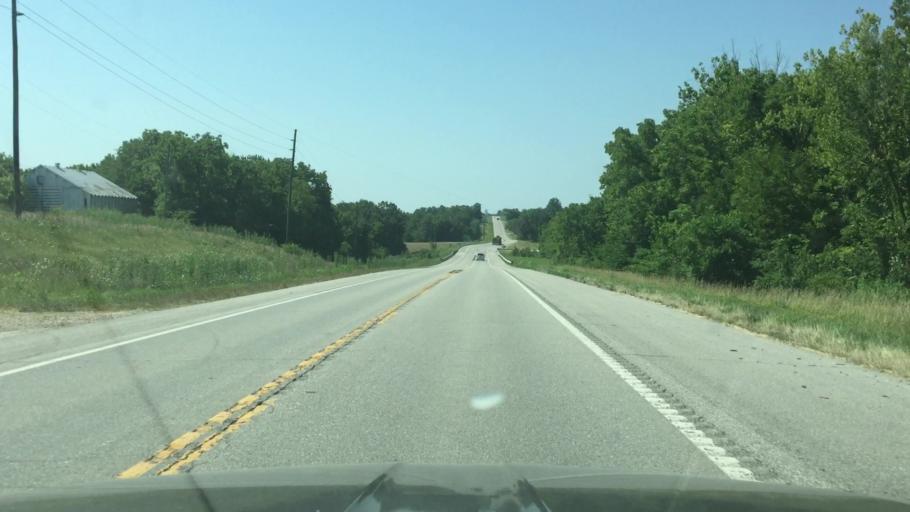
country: US
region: Missouri
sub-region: Moniteau County
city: Tipton
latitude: 38.6333
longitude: -92.7892
